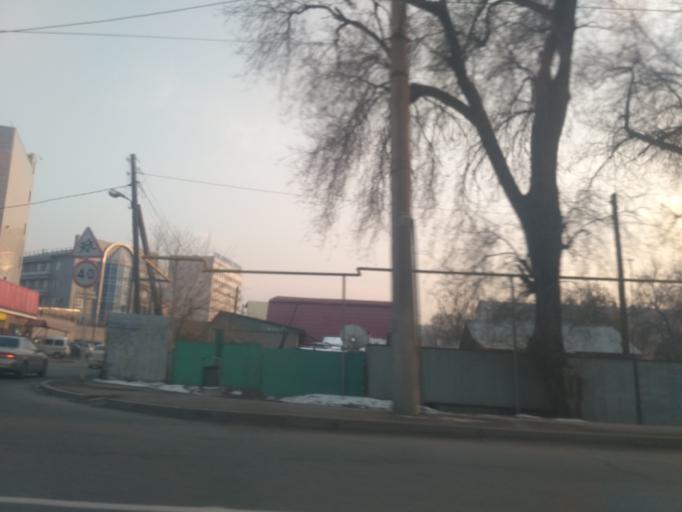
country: KZ
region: Almaty Qalasy
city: Almaty
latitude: 43.2521
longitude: 76.8575
